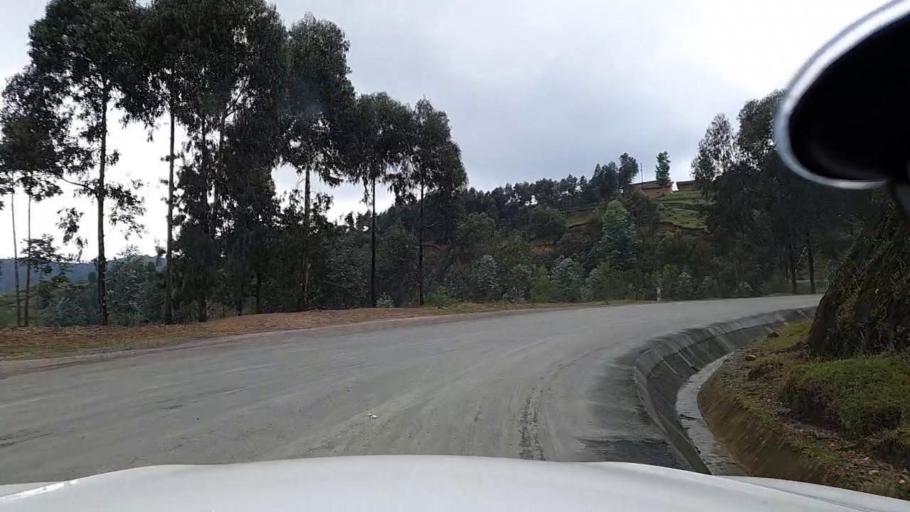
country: RW
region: Western Province
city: Kibuye
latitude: -2.0572
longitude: 29.5178
